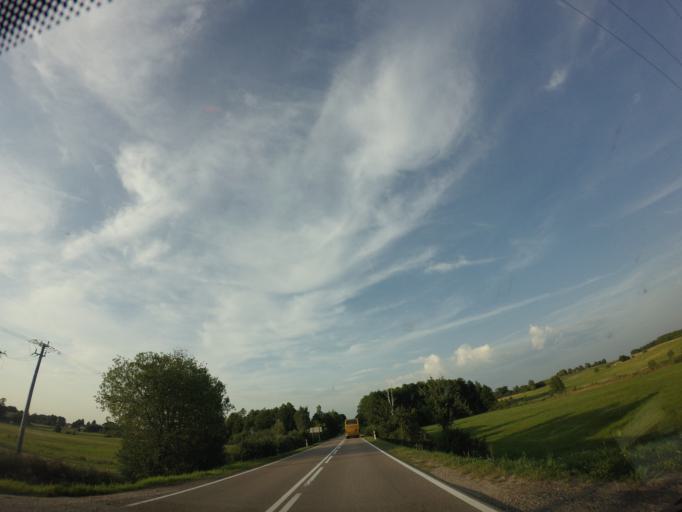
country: PL
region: Podlasie
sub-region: Powiat sejnenski
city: Sejny
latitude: 54.0871
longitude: 23.3840
